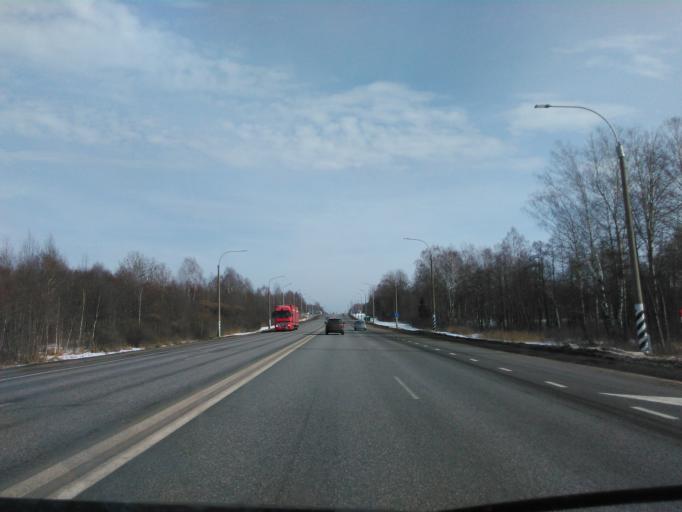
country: RU
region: Smolensk
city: Rudnya
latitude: 54.6903
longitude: 30.9578
